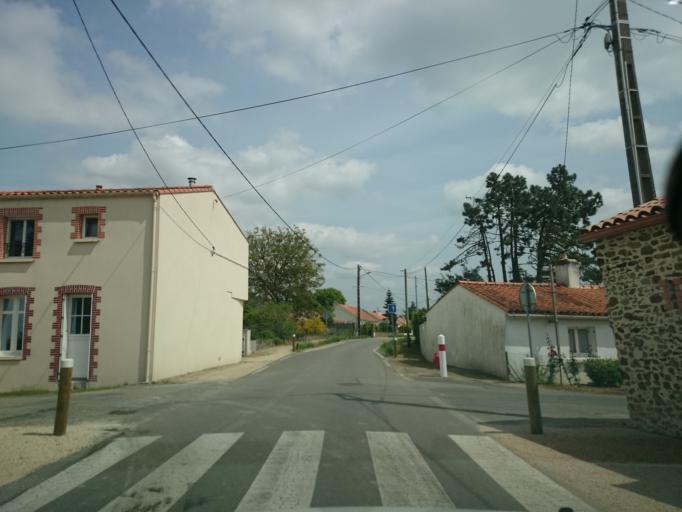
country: FR
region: Pays de la Loire
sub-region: Departement de la Loire-Atlantique
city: Bouaye
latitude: 47.1260
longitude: -1.6462
